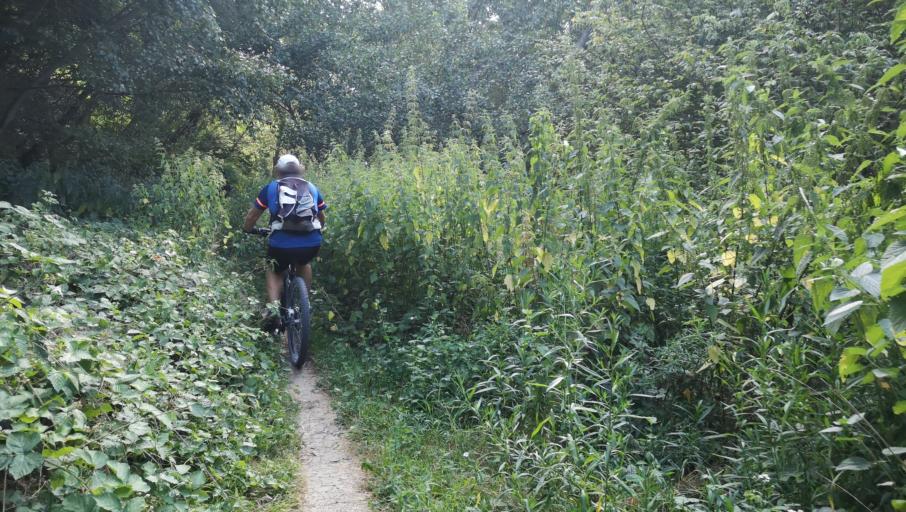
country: FR
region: Centre
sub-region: Departement du Loiret
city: Darvoy
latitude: 47.8737
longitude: 2.1039
